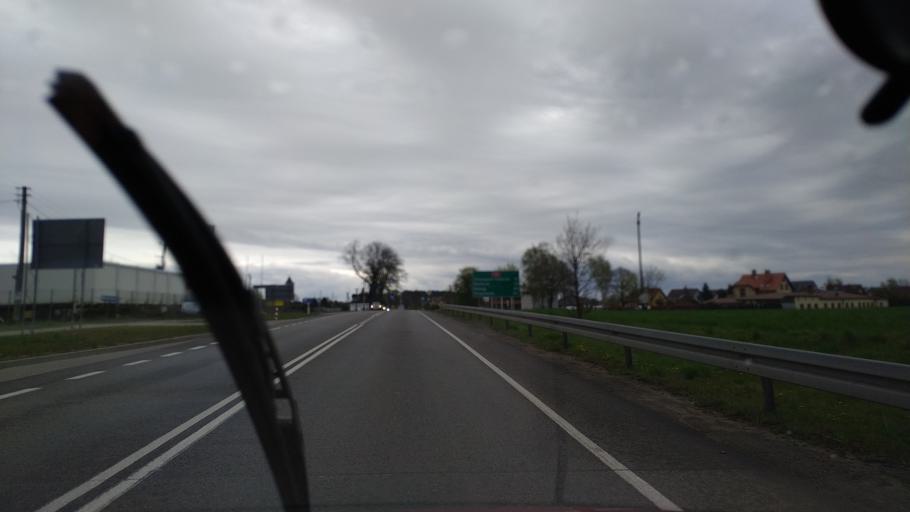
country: PL
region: Pomeranian Voivodeship
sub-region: Powiat starogardzki
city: Zblewo
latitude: 53.9328
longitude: 18.3387
